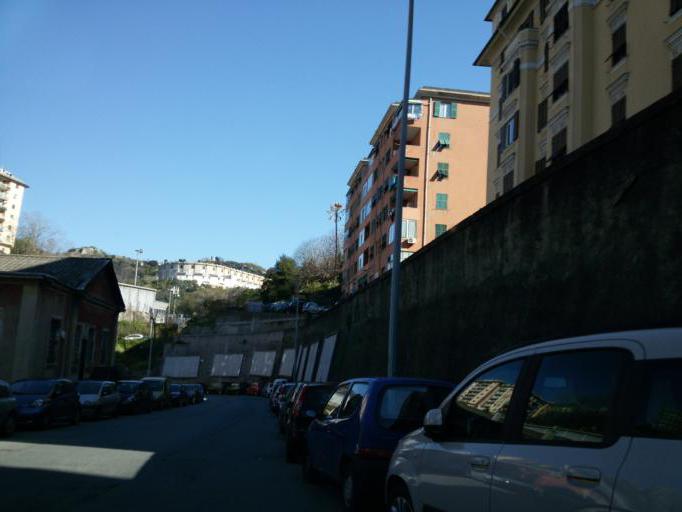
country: IT
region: Liguria
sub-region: Provincia di Genova
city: San Teodoro
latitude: 44.4150
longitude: 8.9028
